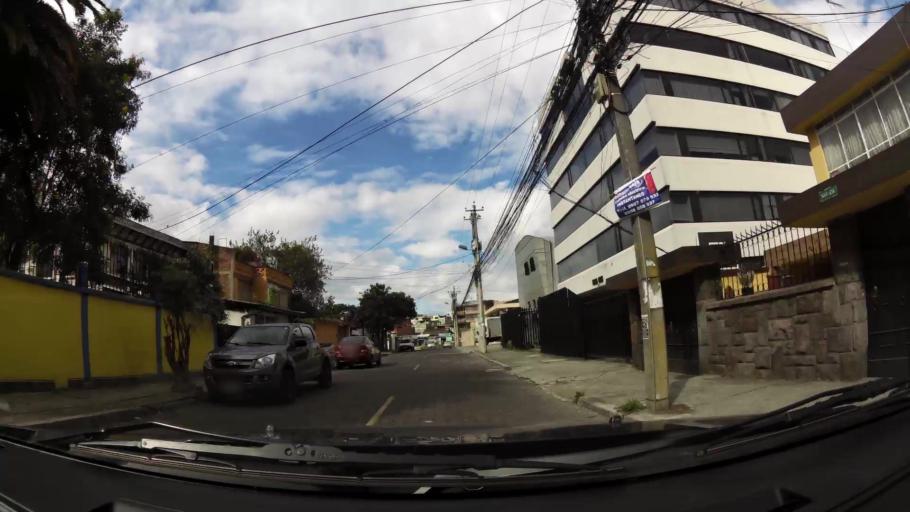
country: EC
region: Pichincha
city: Quito
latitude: -0.1587
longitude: -78.4784
